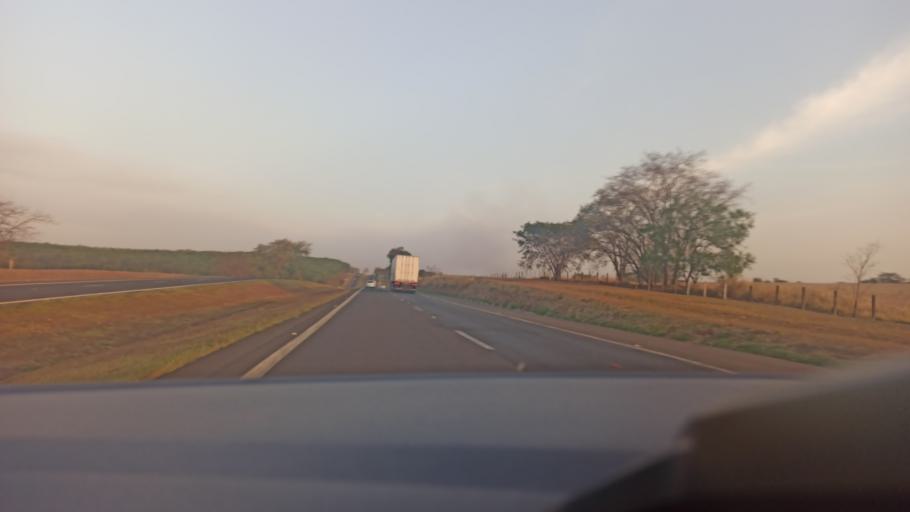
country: BR
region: Sao Paulo
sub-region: Taquaritinga
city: Taquaritinga
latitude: -21.4470
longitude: -48.6401
